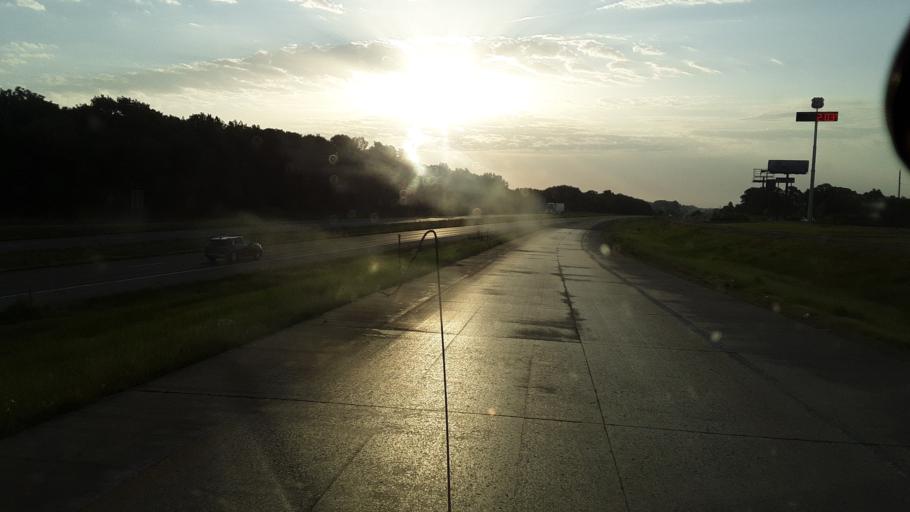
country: US
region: Missouri
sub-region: Callaway County
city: Fulton
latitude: 38.9437
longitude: -91.9393
